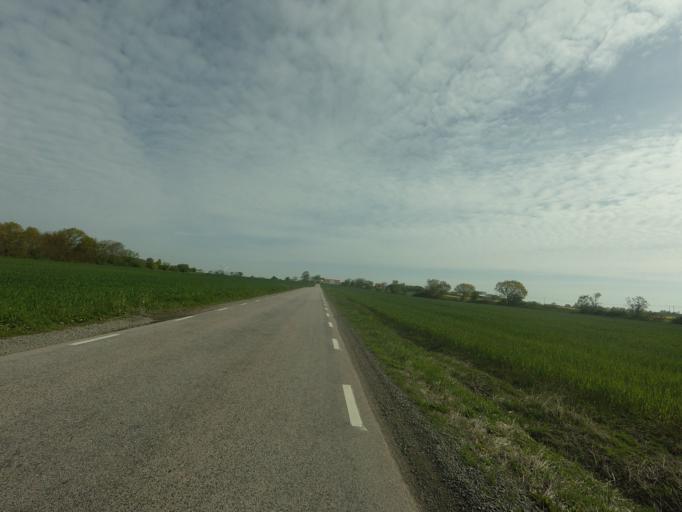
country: SE
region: Skane
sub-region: Hoganas Kommun
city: Hoganas
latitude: 56.2073
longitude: 12.5783
